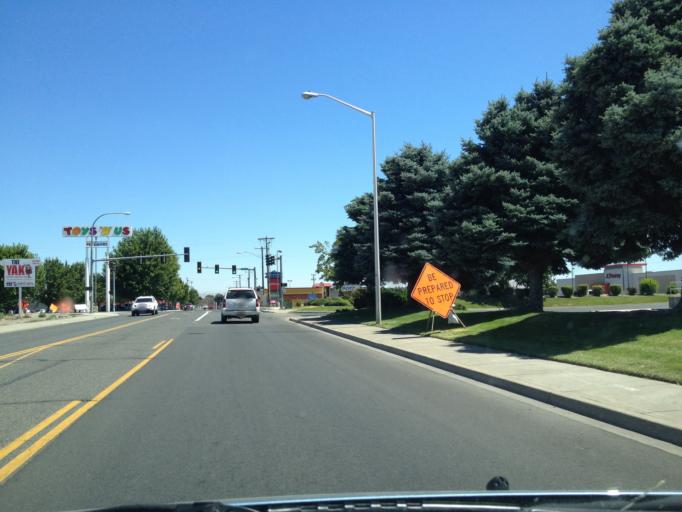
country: US
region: Washington
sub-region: Yakima County
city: Union Gap
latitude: 46.5704
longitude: -120.4841
